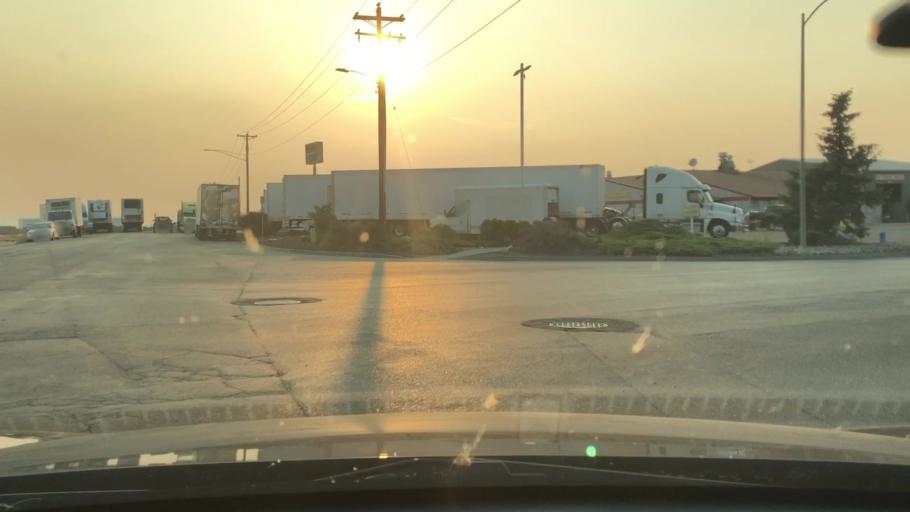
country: US
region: Washington
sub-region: Franklin County
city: Pasco
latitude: 46.2629
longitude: -119.0838
